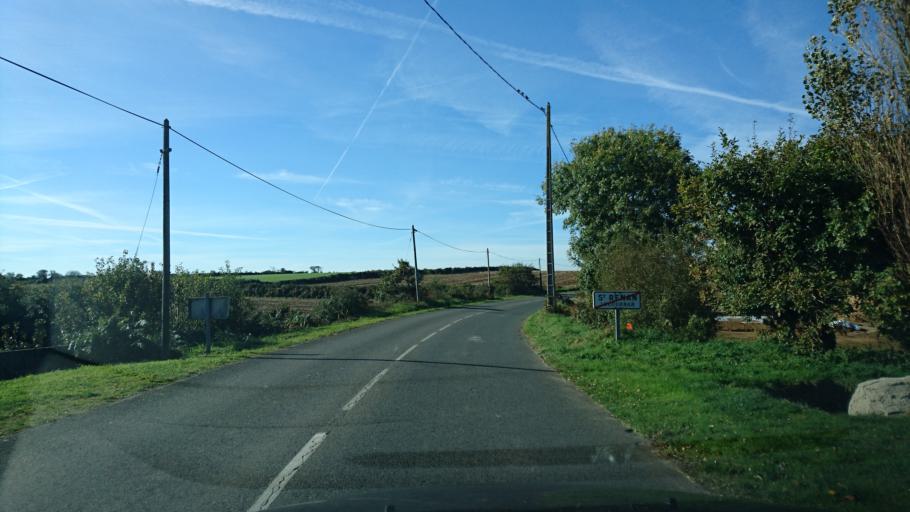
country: FR
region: Brittany
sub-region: Departement du Finistere
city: Saint-Renan
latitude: 48.4305
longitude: -4.6332
